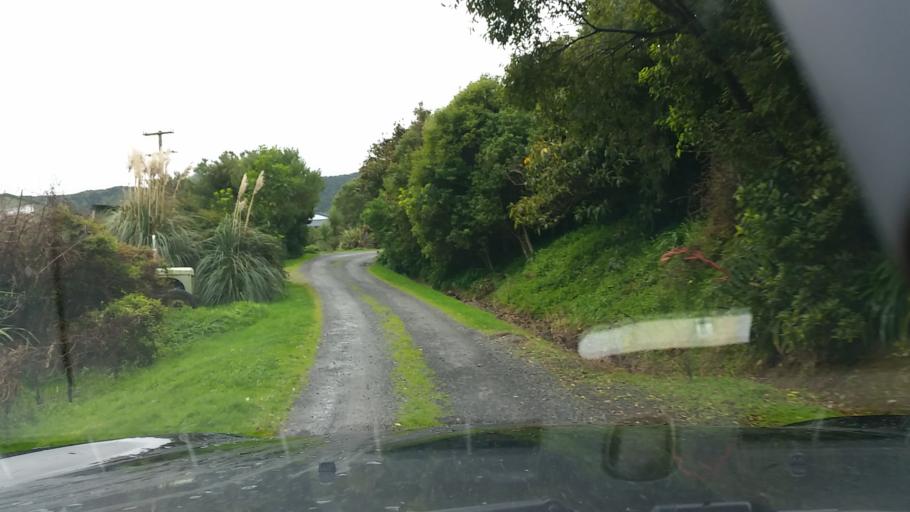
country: NZ
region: Marlborough
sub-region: Marlborough District
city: Picton
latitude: -41.2705
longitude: 174.0768
